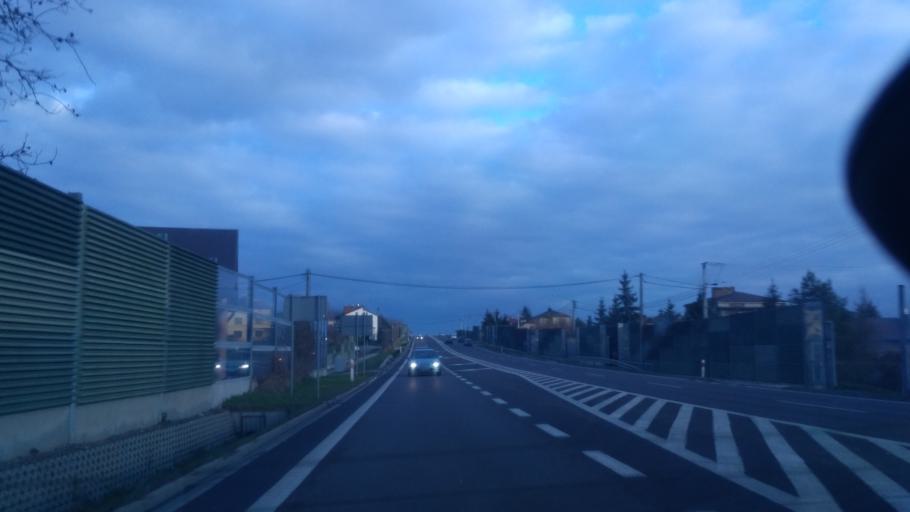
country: PL
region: Subcarpathian Voivodeship
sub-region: Powiat rzeszowski
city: Krasne
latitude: 50.0417
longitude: 22.0999
